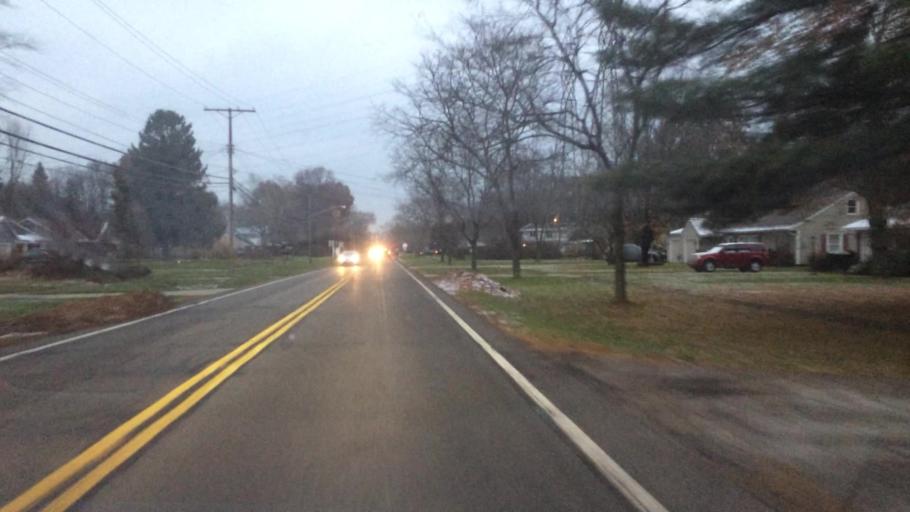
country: US
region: Ohio
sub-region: Cuyahoga County
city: Berea
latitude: 41.3670
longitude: -81.8779
